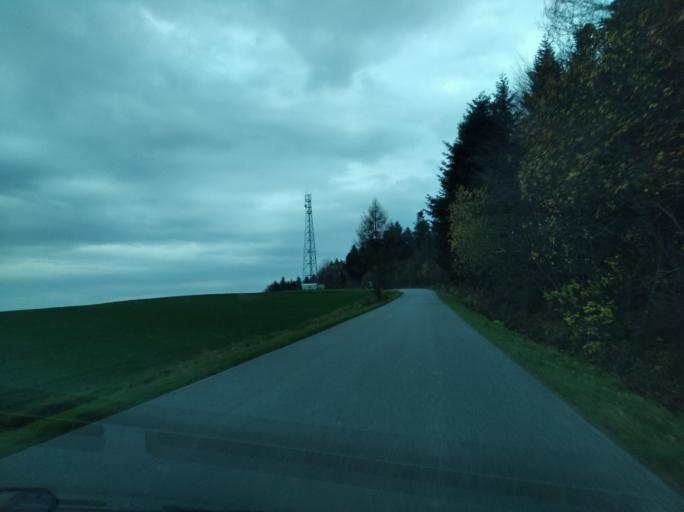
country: PL
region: Subcarpathian Voivodeship
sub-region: Powiat ropczycko-sedziszowski
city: Zagorzyce
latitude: 49.9580
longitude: 21.6935
